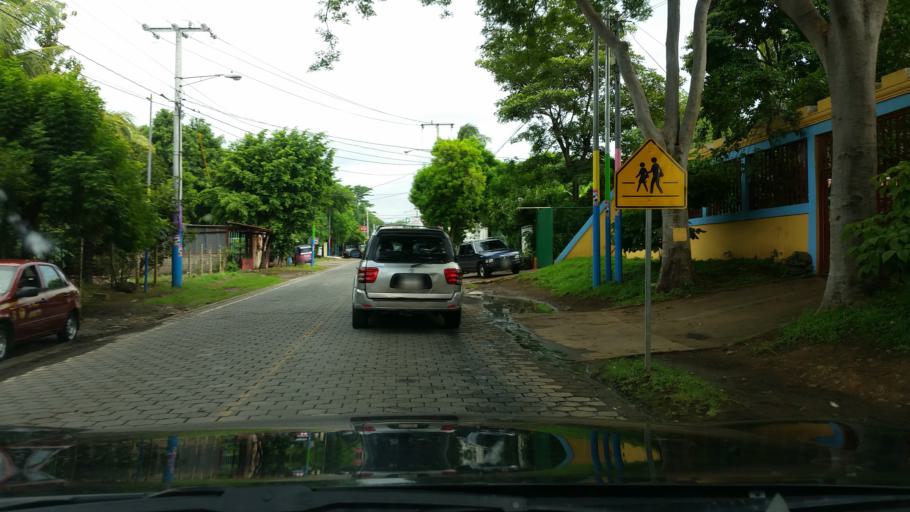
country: NI
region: Masaya
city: Ticuantepe
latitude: 12.0506
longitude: -86.2027
